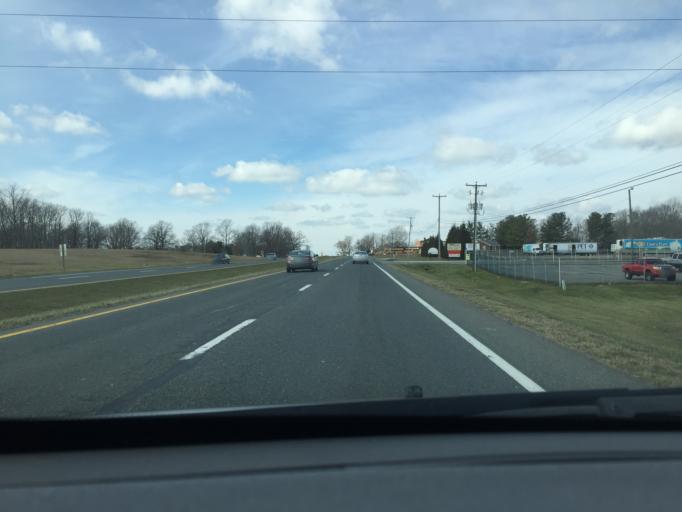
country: US
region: Virginia
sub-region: Campbell County
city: Timberlake
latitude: 37.3057
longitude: -79.3008
